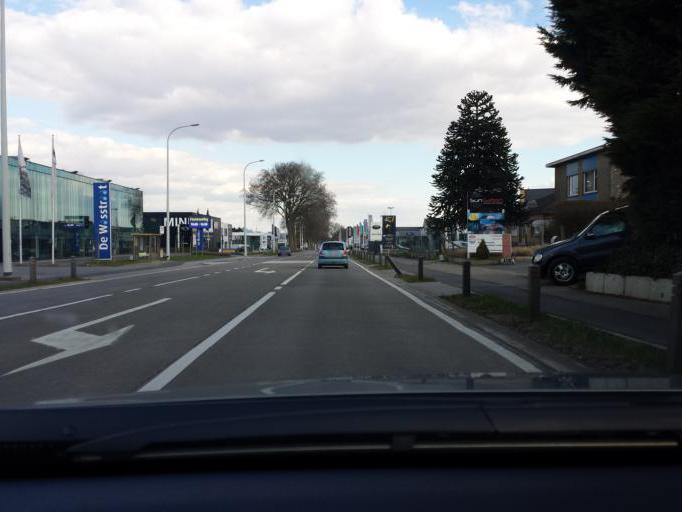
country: BE
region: Flanders
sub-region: Provincie Vlaams-Brabant
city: Herent
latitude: 50.8884
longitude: 4.6595
